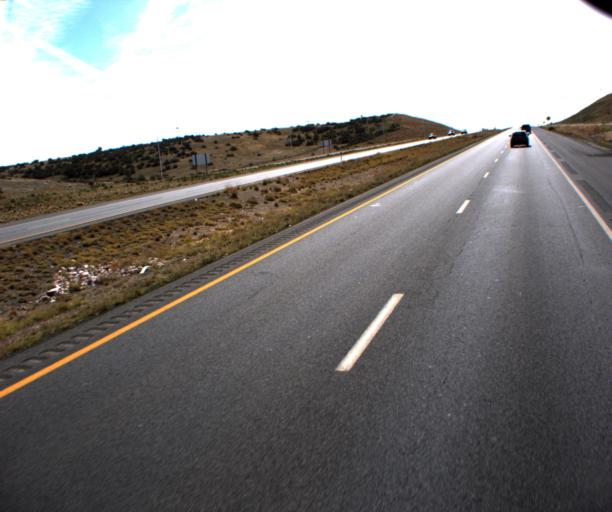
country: US
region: Arizona
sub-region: Yavapai County
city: Prescott Valley
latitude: 34.6355
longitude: -112.3975
